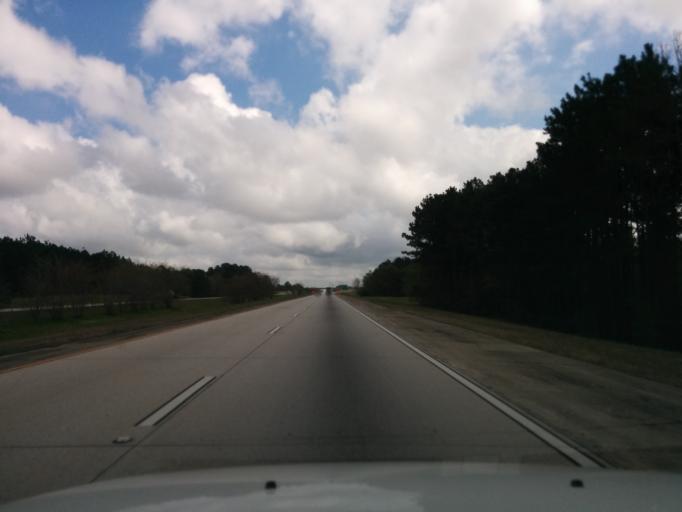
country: US
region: Georgia
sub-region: Evans County
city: Claxton
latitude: 32.3098
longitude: -81.8855
